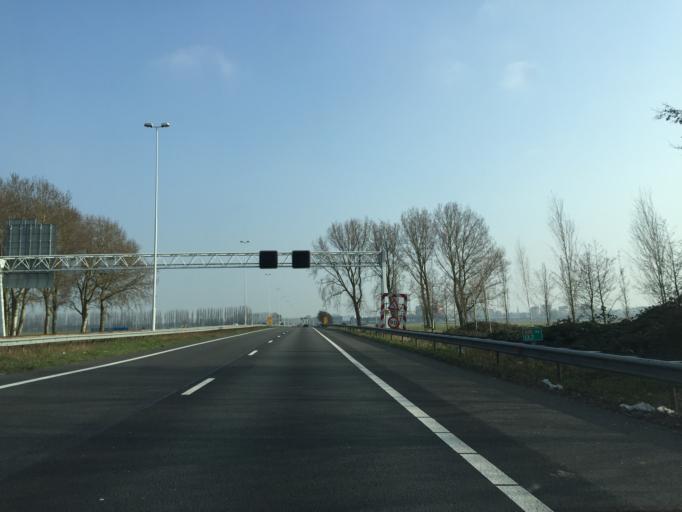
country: NL
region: South Holland
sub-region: Gemeente Maassluis
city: Maassluis
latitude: 51.9440
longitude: 4.2393
